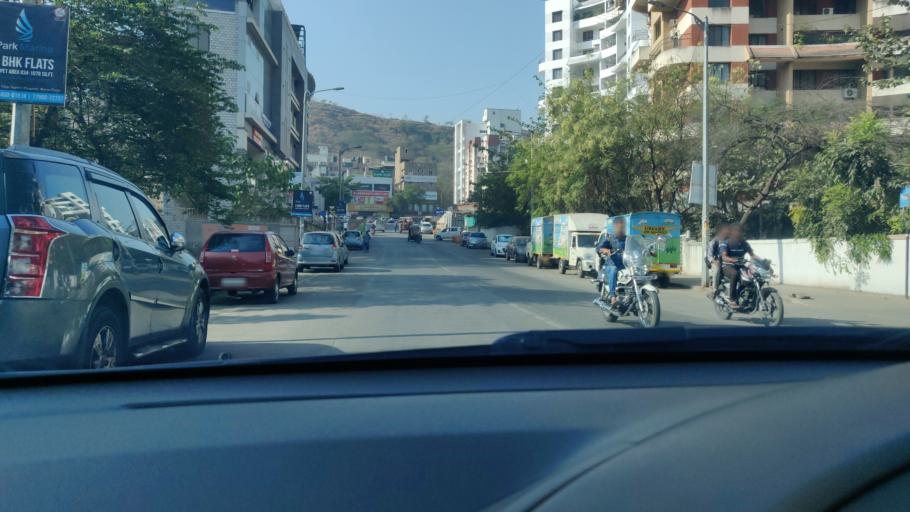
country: IN
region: Maharashtra
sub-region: Pune Division
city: Khadki
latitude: 18.5598
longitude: 73.7927
